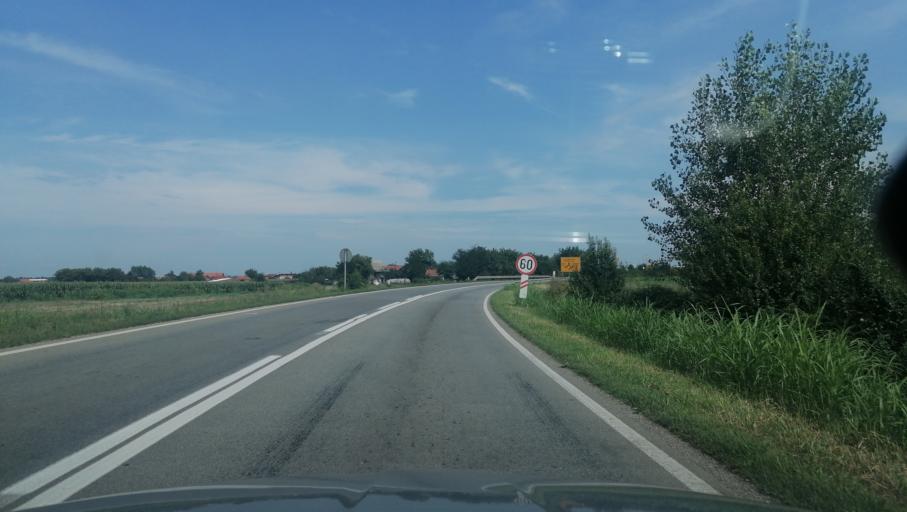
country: BA
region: Republika Srpska
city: Bijeljina
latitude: 44.7820
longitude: 19.2306
